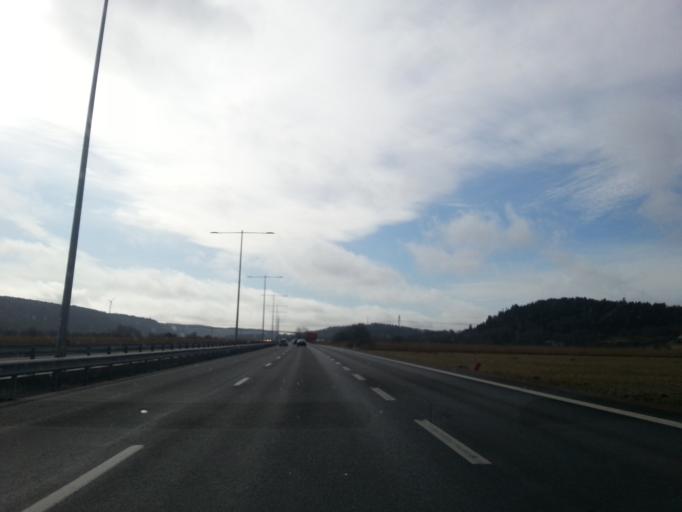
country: SE
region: Vaestra Goetaland
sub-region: Ale Kommun
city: Surte
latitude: 57.8231
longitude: 12.0040
